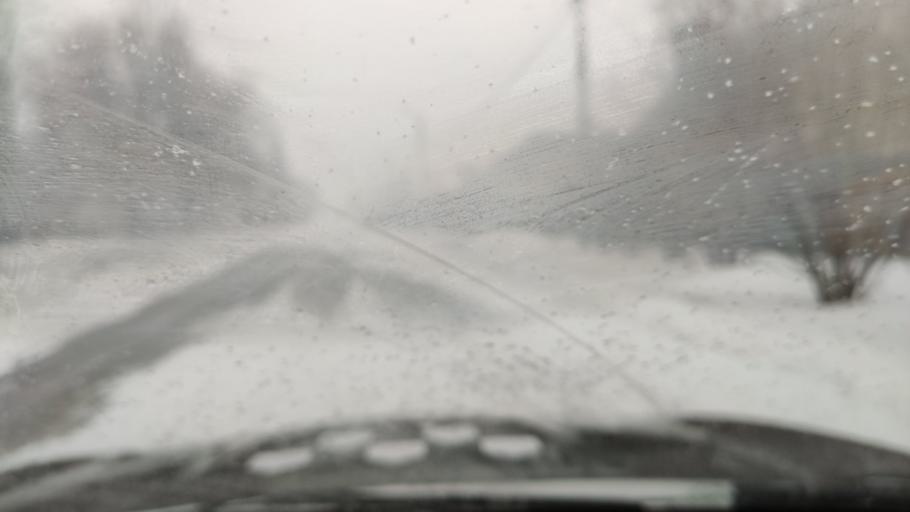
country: RU
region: Samara
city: Povolzhskiy
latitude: 53.5899
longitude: 49.7612
